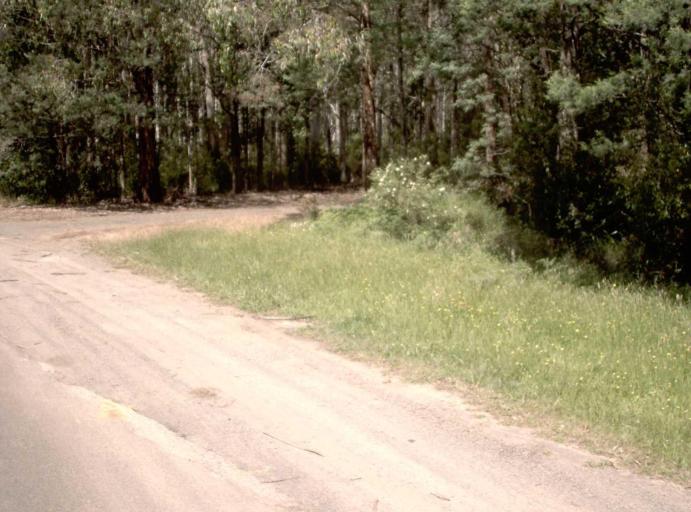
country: AU
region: Victoria
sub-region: Baw Baw
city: Warragul
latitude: -37.8619
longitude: 146.1062
